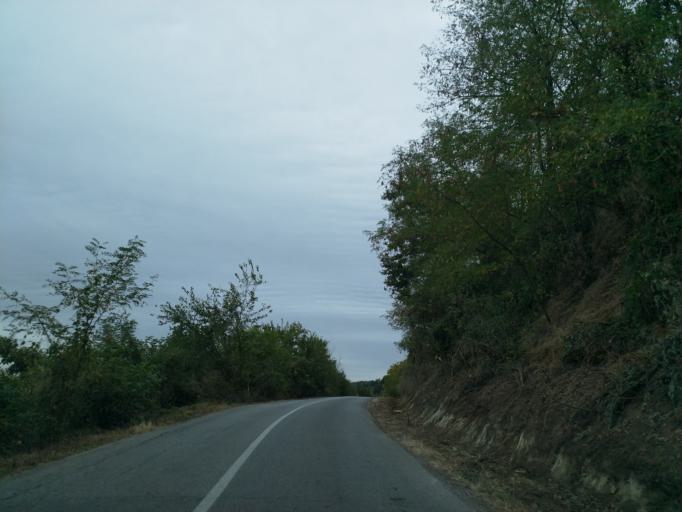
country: RS
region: Central Serbia
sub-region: Pomoravski Okrug
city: Paracin
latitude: 43.8540
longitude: 21.3240
